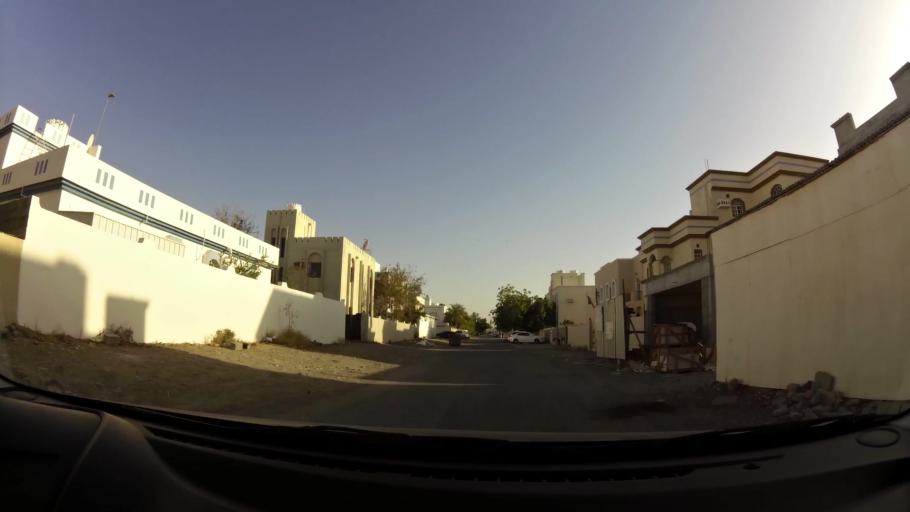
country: OM
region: Muhafazat Masqat
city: As Sib al Jadidah
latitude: 23.6349
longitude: 58.1947
